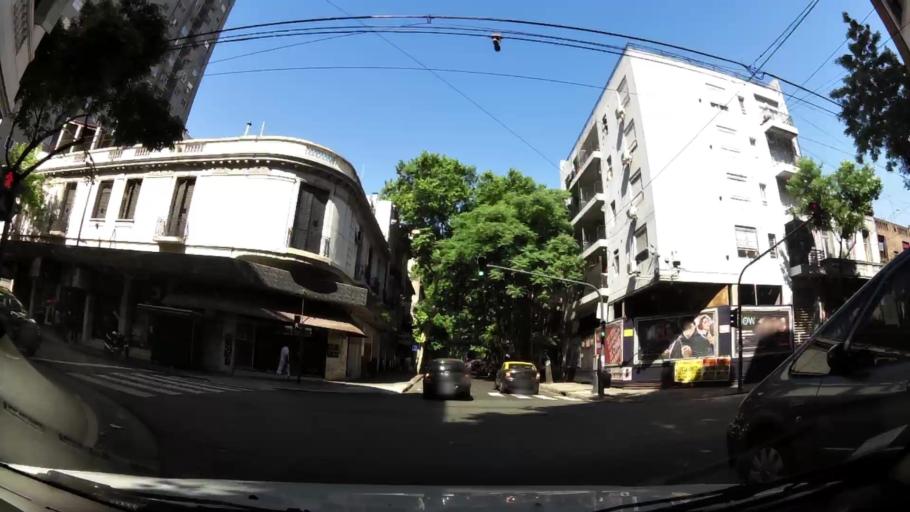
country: AR
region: Buenos Aires F.D.
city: Buenos Aires
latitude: -34.6116
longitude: -58.4103
